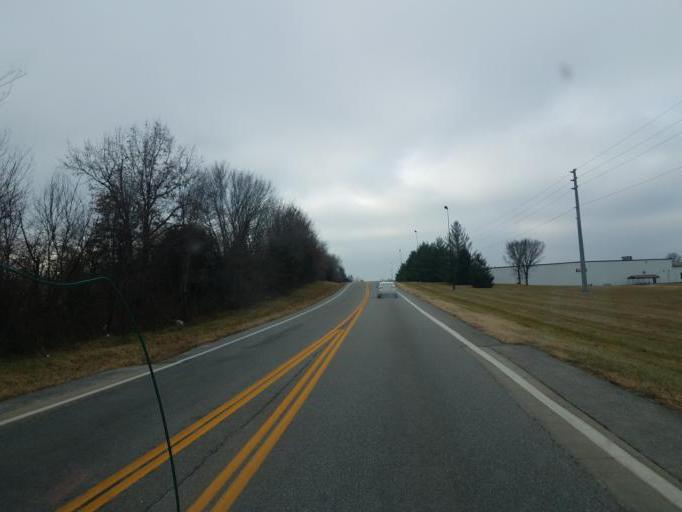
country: US
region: Missouri
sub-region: Greene County
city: Strafford
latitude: 37.2437
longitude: -93.1953
